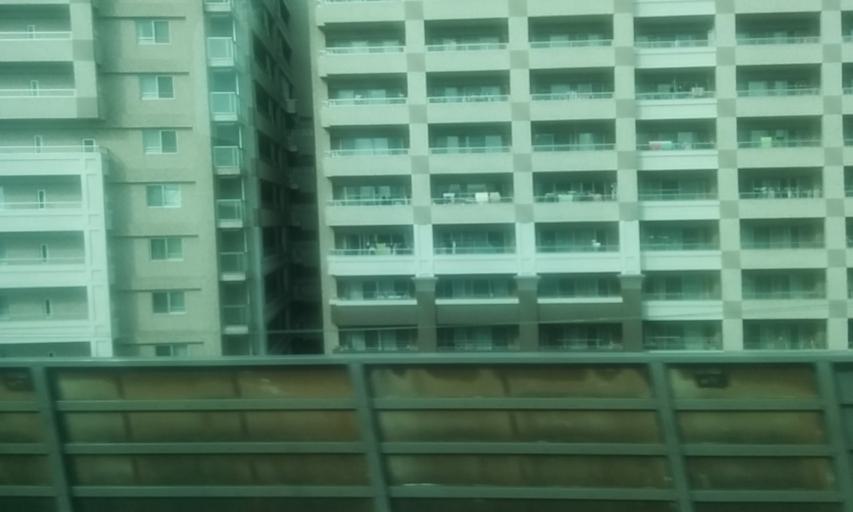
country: JP
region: Kanagawa
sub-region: Kawasaki-shi
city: Kawasaki
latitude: 35.5370
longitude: 139.6764
